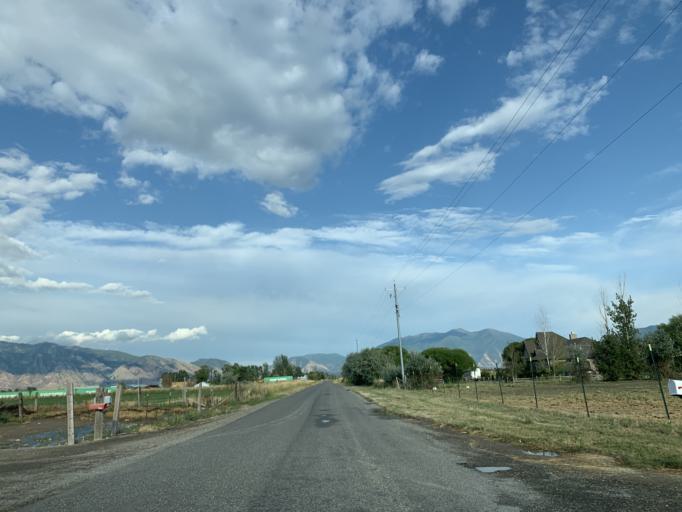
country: US
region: Utah
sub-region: Utah County
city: Benjamin
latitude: 40.1288
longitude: -111.7619
